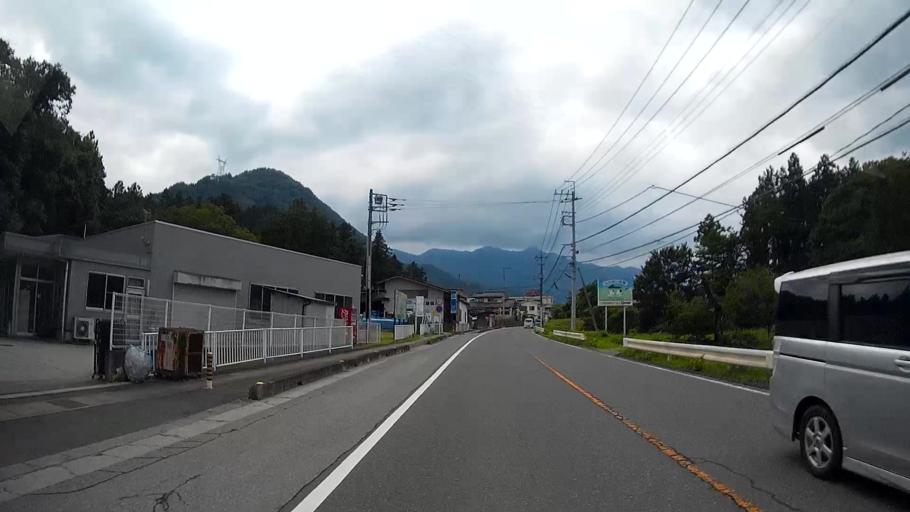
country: JP
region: Saitama
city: Chichibu
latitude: 35.9630
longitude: 139.0522
